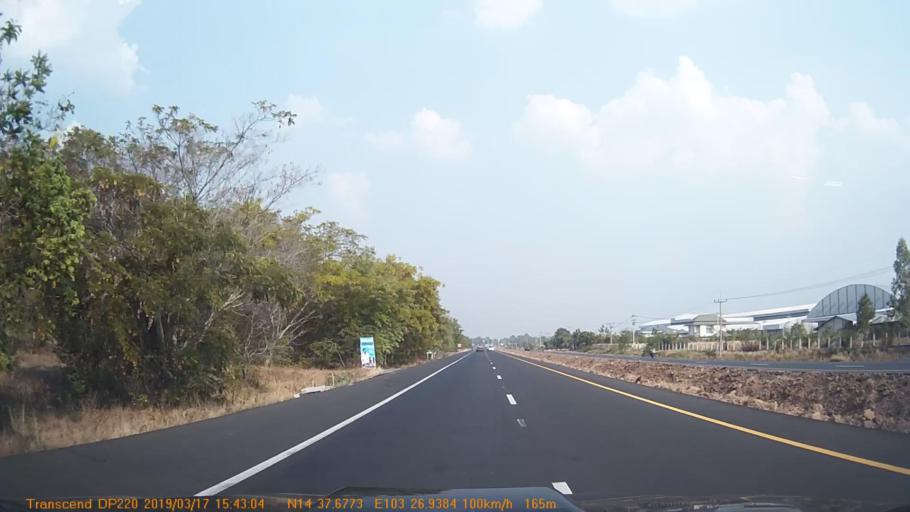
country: TH
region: Surin
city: Prasat
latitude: 14.6278
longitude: 103.4493
